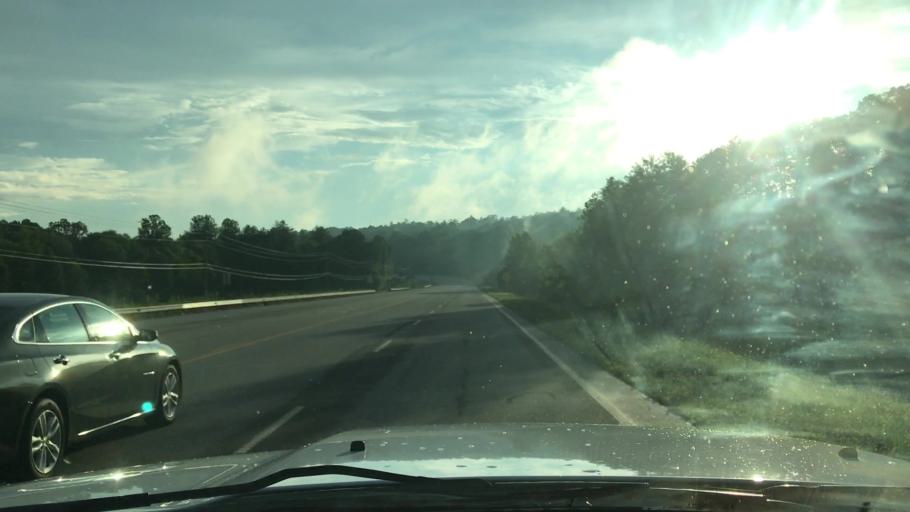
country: US
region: North Carolina
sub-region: Cherokee County
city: Murphy
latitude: 34.9890
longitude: -84.1733
